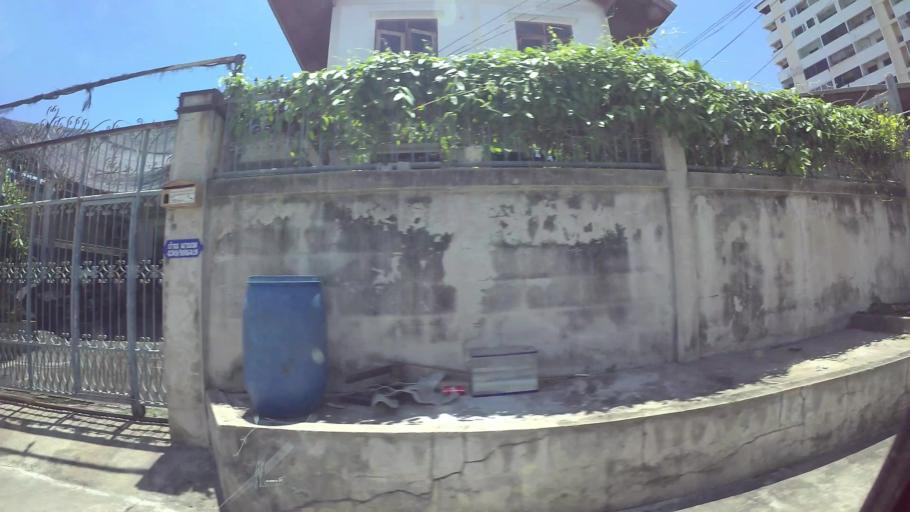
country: TH
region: Chon Buri
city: Phatthaya
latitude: 12.9305
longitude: 100.8957
